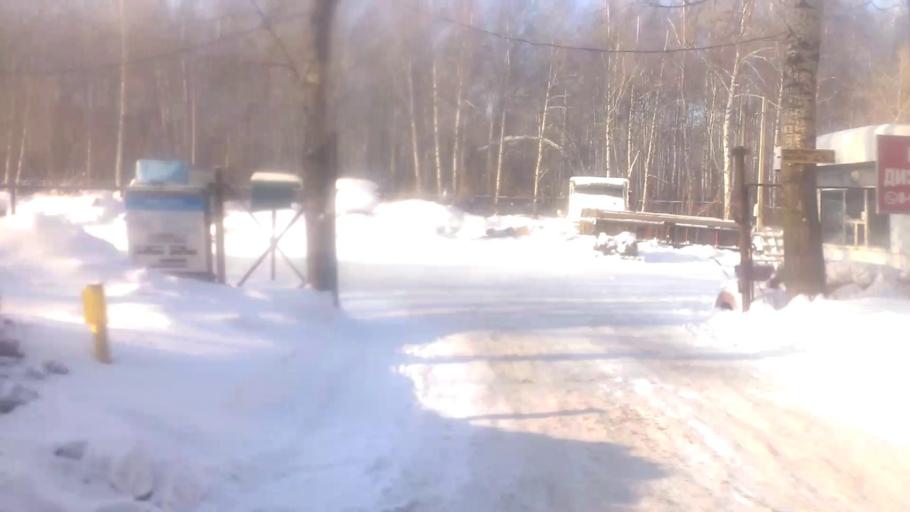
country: RU
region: Altai Krai
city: Novosilikatnyy
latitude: 53.3729
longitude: 83.6625
